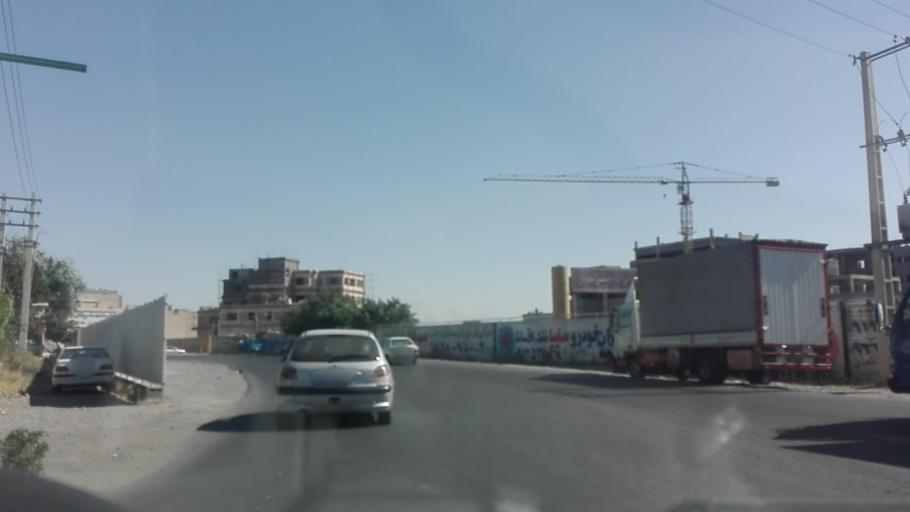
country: IR
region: Tehran
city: Shahriar
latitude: 35.6417
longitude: 51.0633
